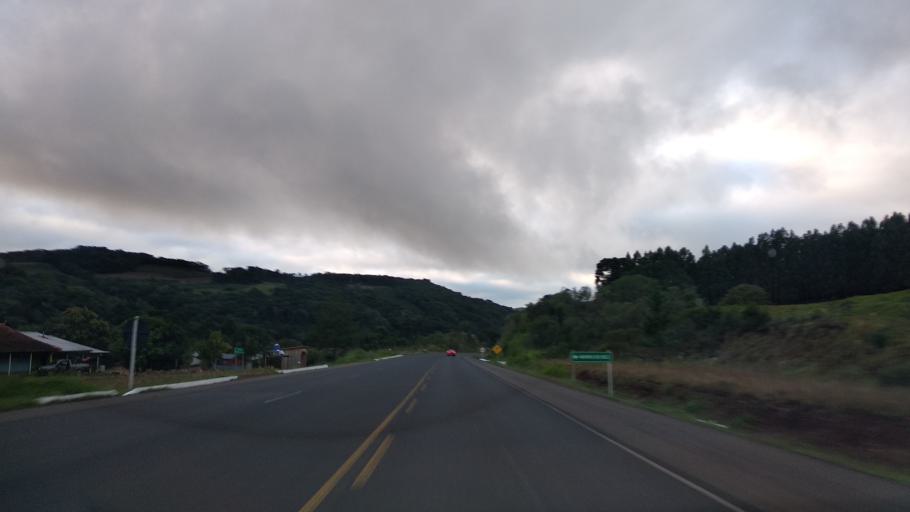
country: BR
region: Santa Catarina
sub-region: Campos Novos
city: Campos Novos
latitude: -27.4519
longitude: -50.9936
